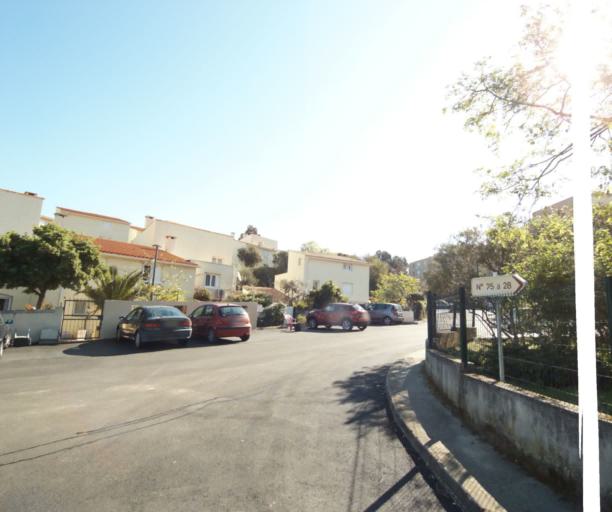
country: FR
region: Corsica
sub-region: Departement de la Corse-du-Sud
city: Propriano
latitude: 41.6682
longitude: 8.8977
